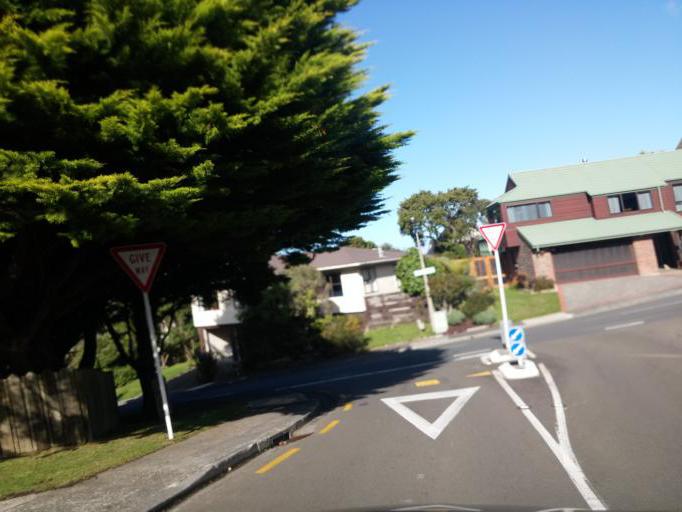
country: NZ
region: Wellington
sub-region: Wellington City
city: Kelburn
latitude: -41.2430
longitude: 174.7805
